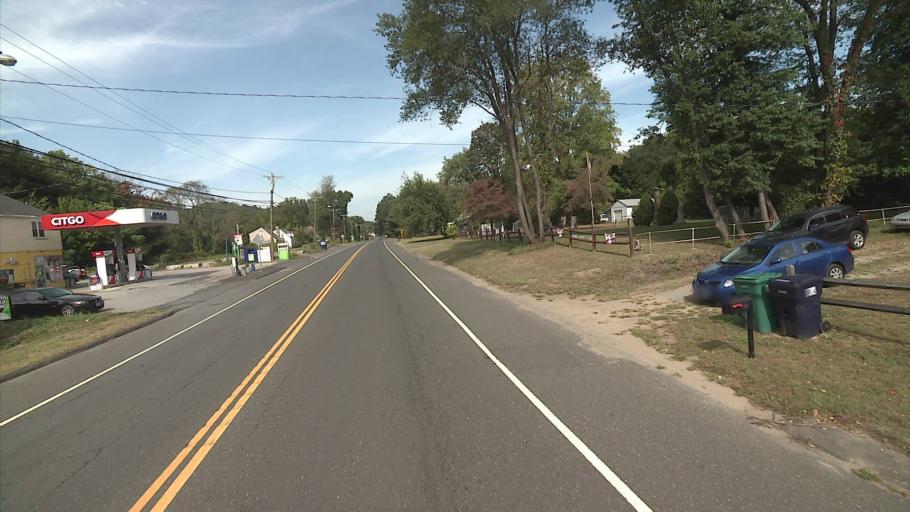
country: US
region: Connecticut
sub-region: New Haven County
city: Ansonia
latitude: 41.3674
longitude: -73.1453
